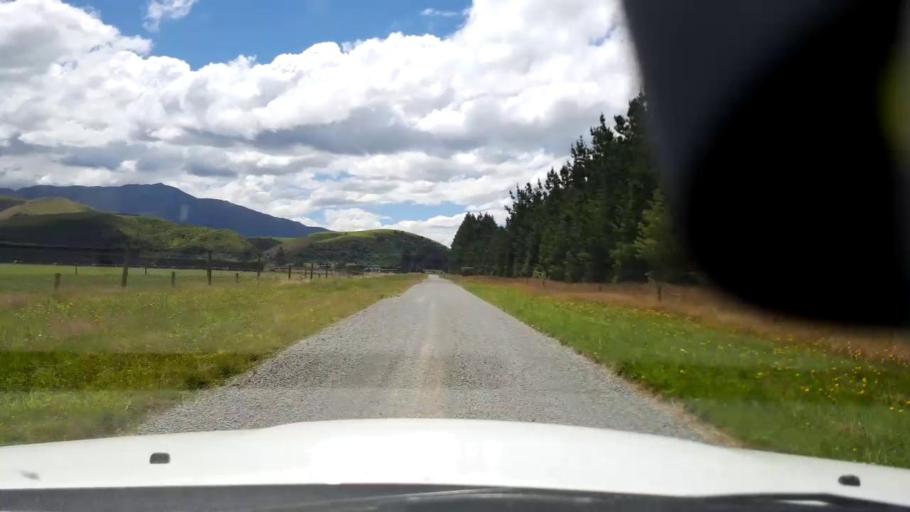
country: NZ
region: Canterbury
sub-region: Timaru District
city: Pleasant Point
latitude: -43.9644
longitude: 171.2272
